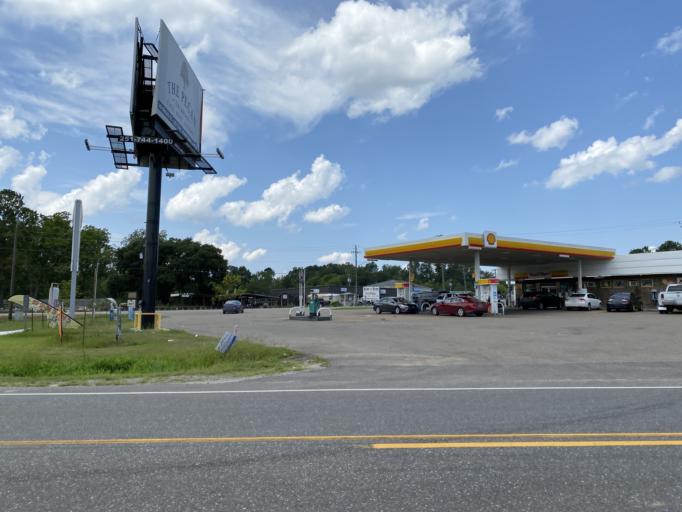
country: US
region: Alabama
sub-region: Wilcox County
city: Camden
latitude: 31.9941
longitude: -87.2780
